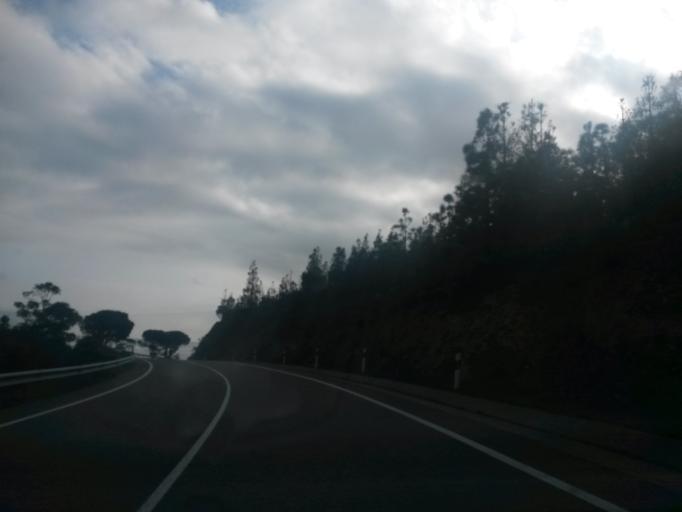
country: ES
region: Catalonia
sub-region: Provincia de Girona
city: Colera
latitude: 42.4089
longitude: 3.1525
